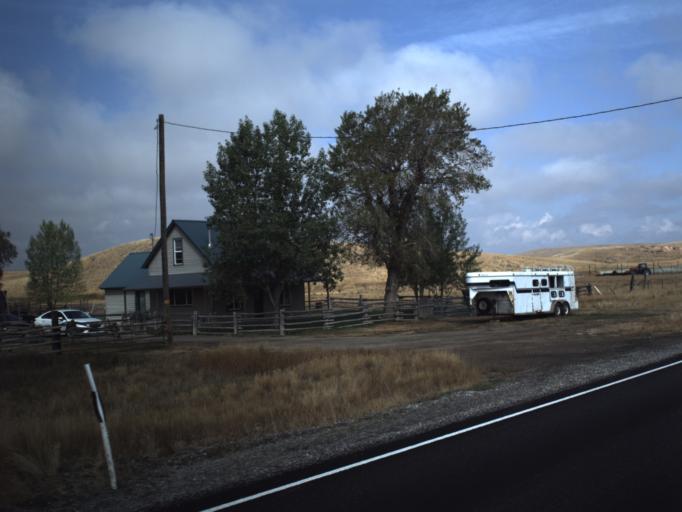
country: US
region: Utah
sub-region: Rich County
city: Randolph
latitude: 41.5322
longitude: -111.1628
